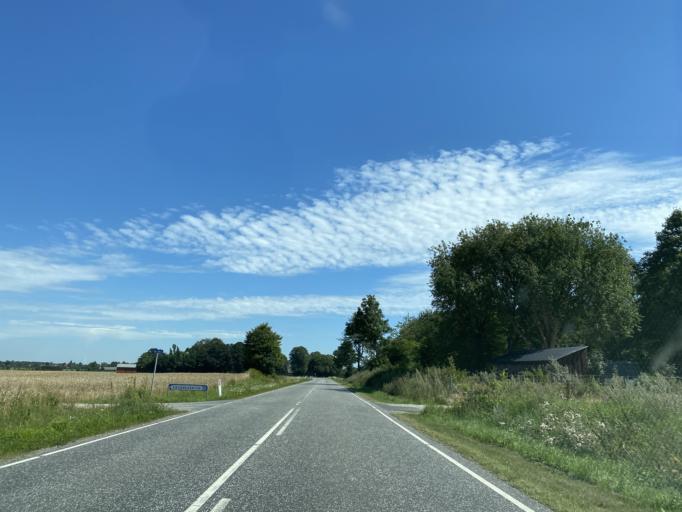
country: DK
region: South Denmark
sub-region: Nyborg Kommune
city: Ullerslev
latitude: 55.2523
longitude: 10.6410
